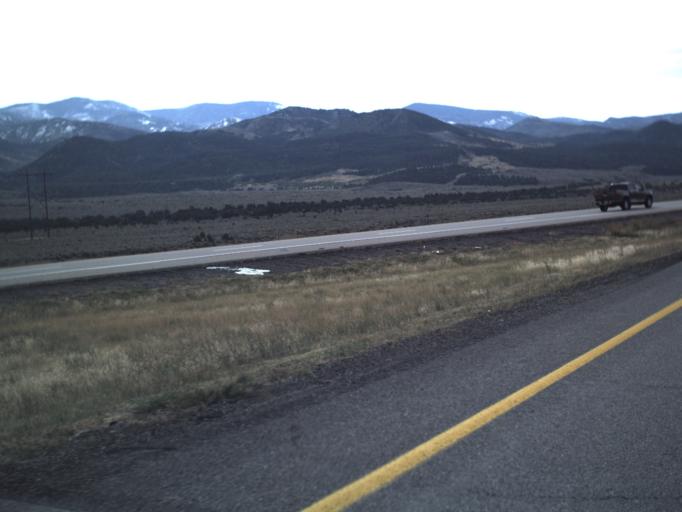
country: US
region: Utah
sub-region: Beaver County
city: Beaver
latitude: 38.5695
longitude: -112.6049
